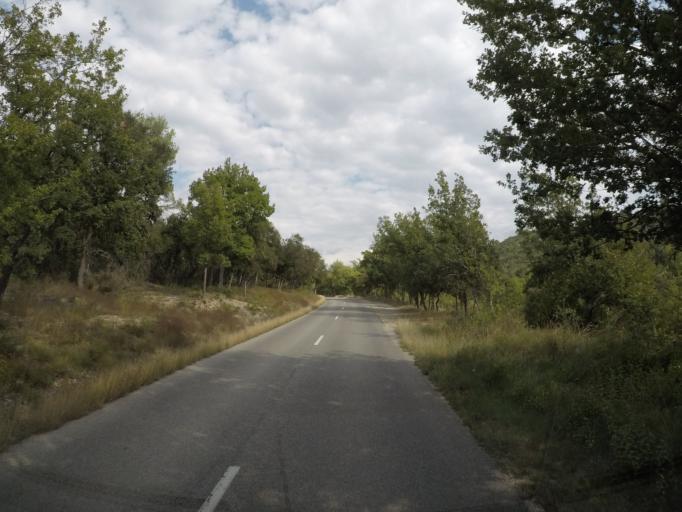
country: FR
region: Provence-Alpes-Cote d'Azur
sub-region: Departement des Alpes-de-Haute-Provence
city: Valensole
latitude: 43.8002
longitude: 5.9425
